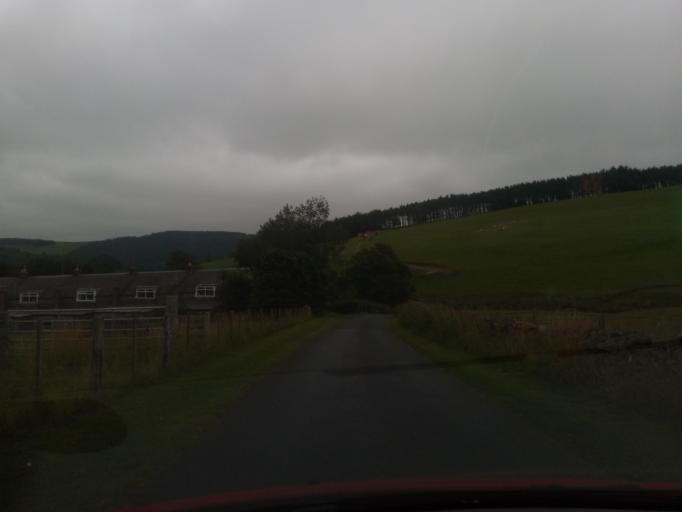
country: GB
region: Scotland
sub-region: Fife
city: Pathhead
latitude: 55.7597
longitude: -2.9353
